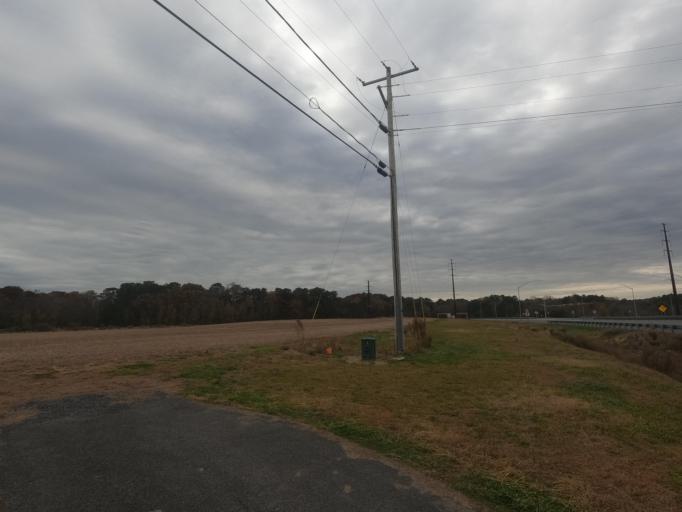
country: US
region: Maryland
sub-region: Worcester County
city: Snow Hill
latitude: 38.1898
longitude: -75.3734
